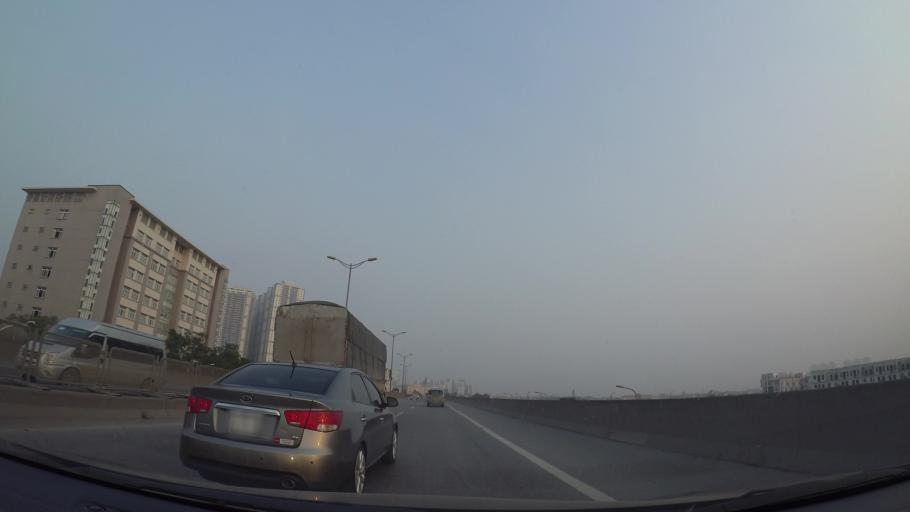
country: VN
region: Ha Noi
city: Thanh Xuan
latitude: 20.9762
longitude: 105.8145
